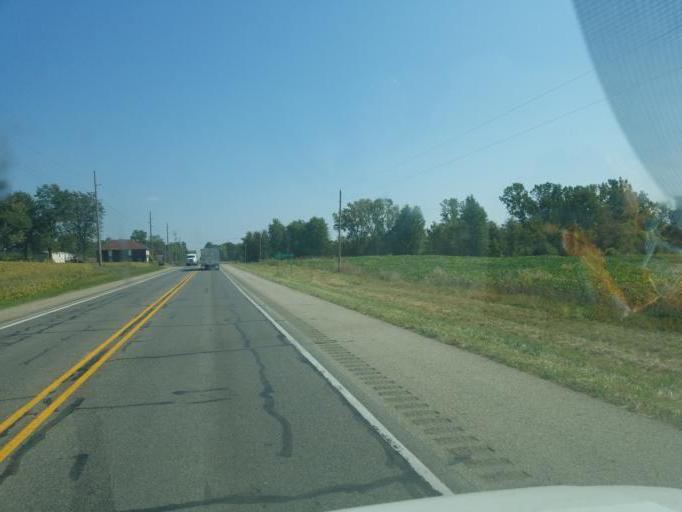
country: US
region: Indiana
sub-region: Steuben County
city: Angola
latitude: 41.6344
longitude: -85.1449
